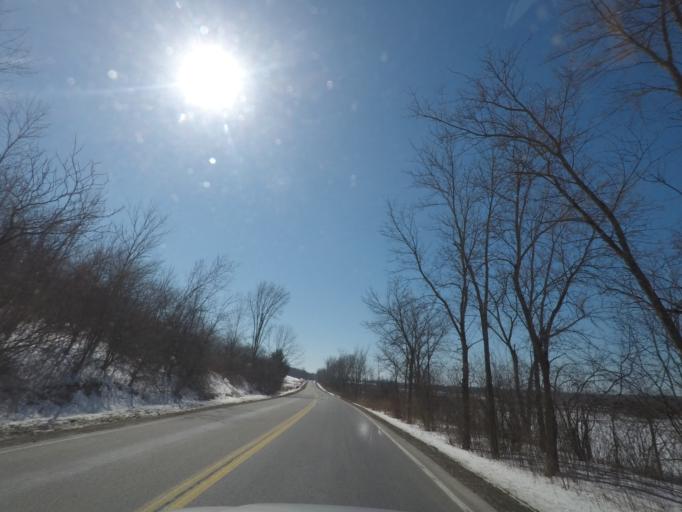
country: US
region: New York
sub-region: Saratoga County
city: Stillwater
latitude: 42.9733
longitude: -73.6162
